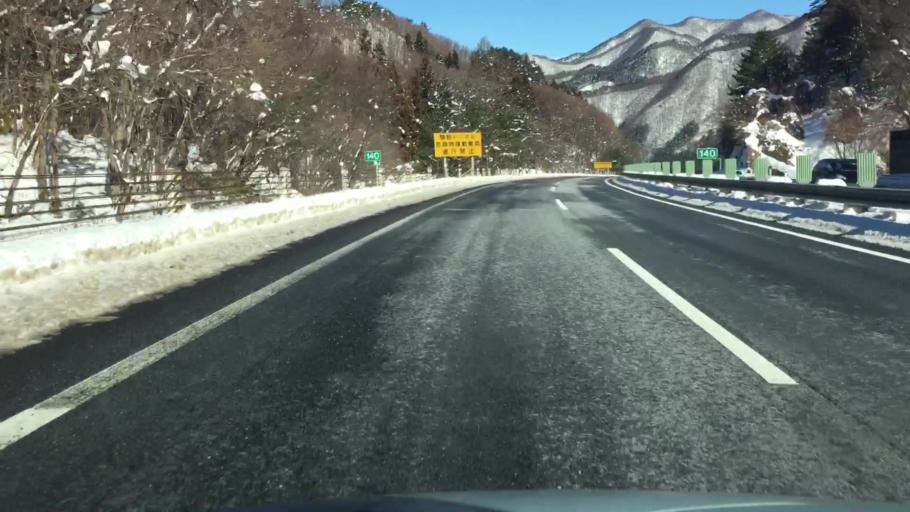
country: JP
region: Gunma
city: Numata
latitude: 36.7370
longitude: 138.9752
